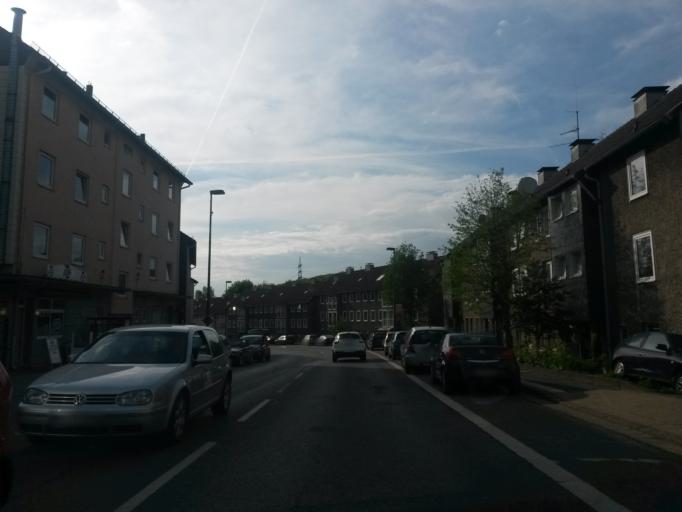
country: DE
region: North Rhine-Westphalia
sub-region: Regierungsbezirk Arnsberg
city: Luedenscheid
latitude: 51.2273
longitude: 7.6444
